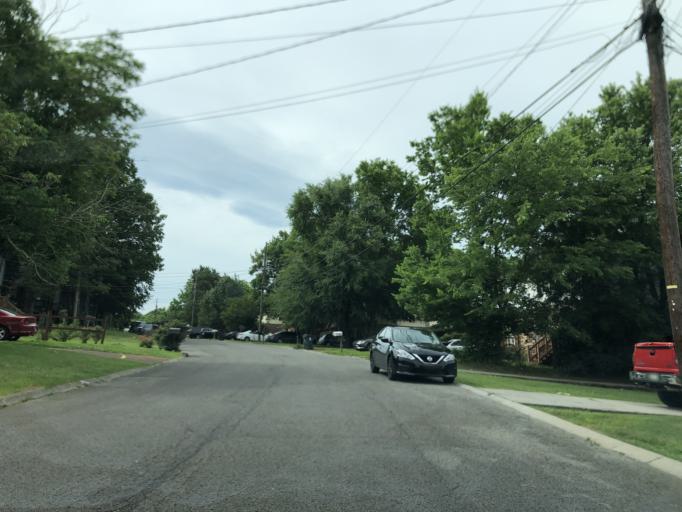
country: US
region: Tennessee
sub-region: Davidson County
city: Goodlettsville
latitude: 36.2844
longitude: -86.7136
